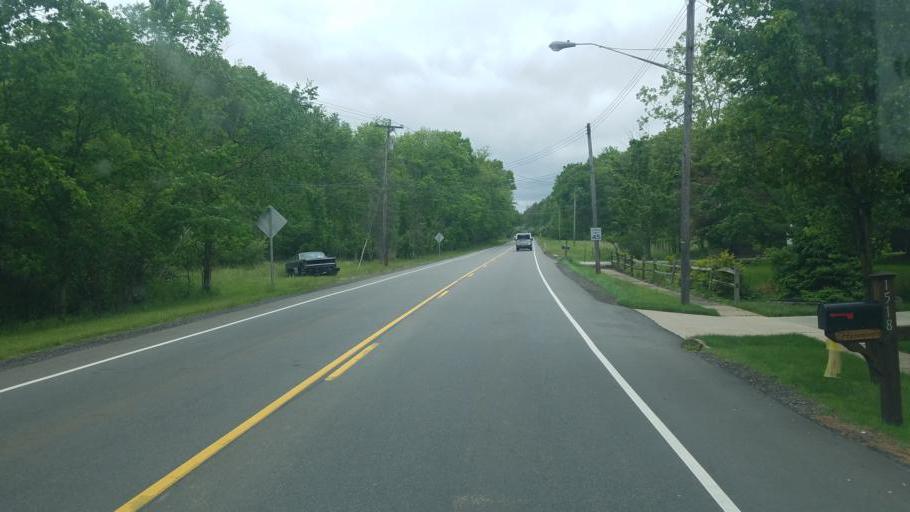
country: US
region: Ohio
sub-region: Summit County
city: Peninsula
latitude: 41.2409
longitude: -81.5457
